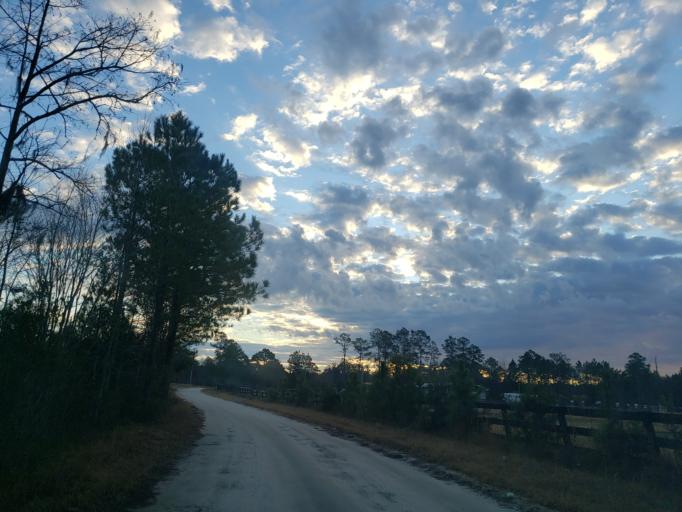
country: US
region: Georgia
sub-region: Chatham County
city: Bloomingdale
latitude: 32.1144
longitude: -81.3490
